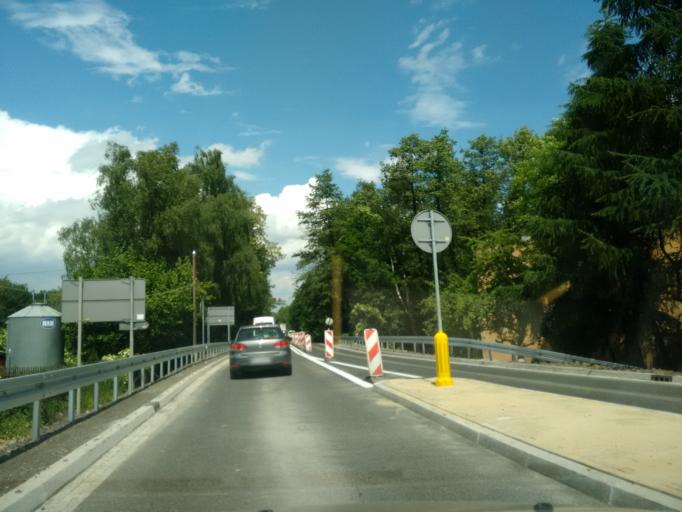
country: PL
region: Silesian Voivodeship
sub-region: Powiat cieszynski
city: Pruchna
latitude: 49.8654
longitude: 18.6820
